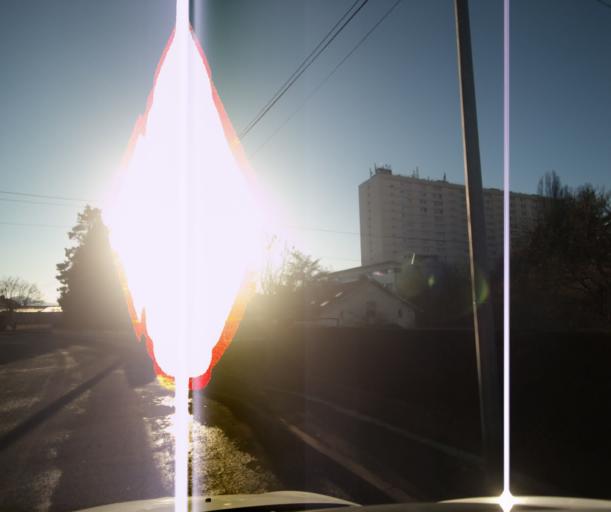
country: FR
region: Franche-Comte
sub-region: Departement du Doubs
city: Besancon
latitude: 47.2552
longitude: 6.0360
